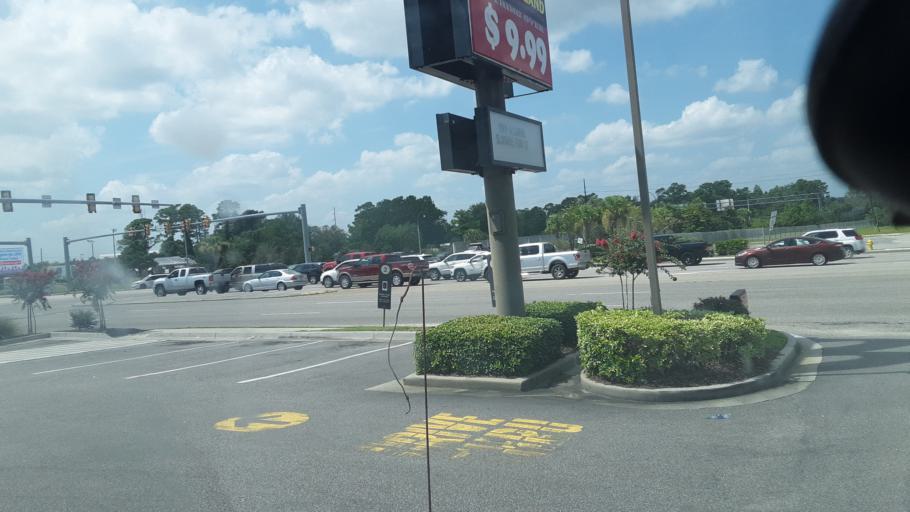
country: US
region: South Carolina
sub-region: Horry County
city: North Myrtle Beach
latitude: 33.8285
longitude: -78.6791
